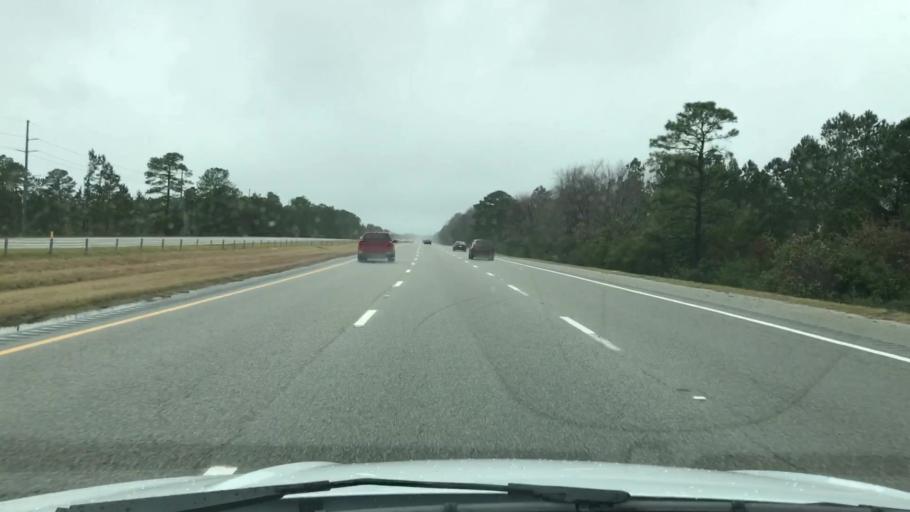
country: US
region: South Carolina
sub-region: Horry County
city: Myrtle Beach
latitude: 33.7498
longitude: -78.8998
